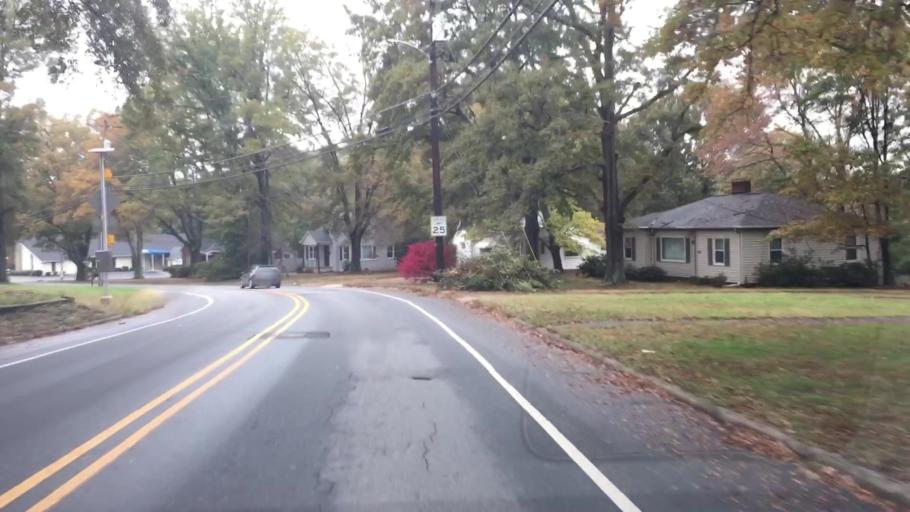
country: US
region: North Carolina
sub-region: Iredell County
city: Mooresville
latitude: 35.5804
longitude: -80.8207
